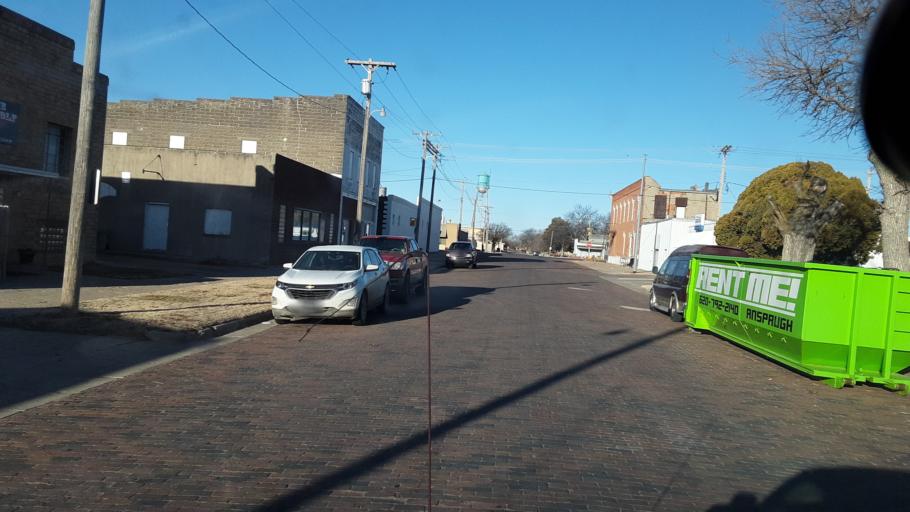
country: US
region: Kansas
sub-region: Barton County
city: Ellinwood
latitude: 38.3546
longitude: -98.5798
